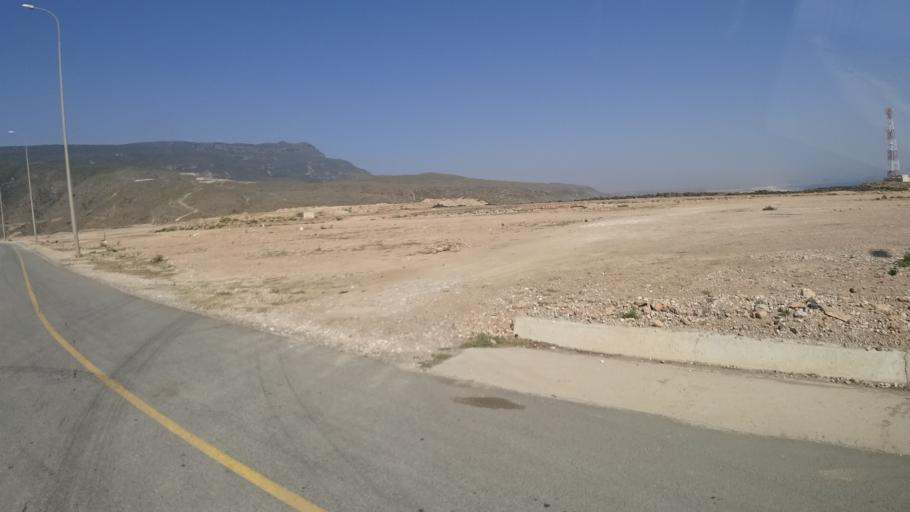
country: OM
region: Zufar
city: Salalah
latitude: 17.0324
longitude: 54.6119
